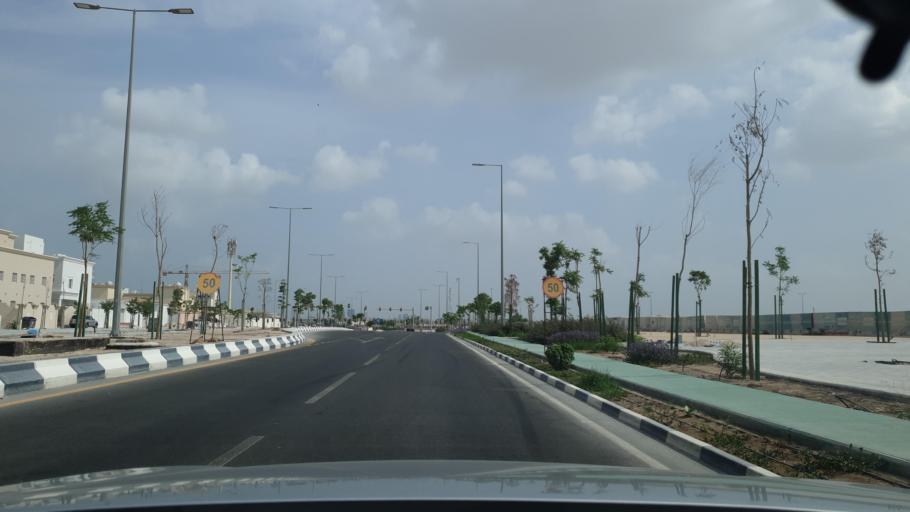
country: QA
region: Baladiyat ar Rayyan
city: Ar Rayyan
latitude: 25.2773
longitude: 51.4584
